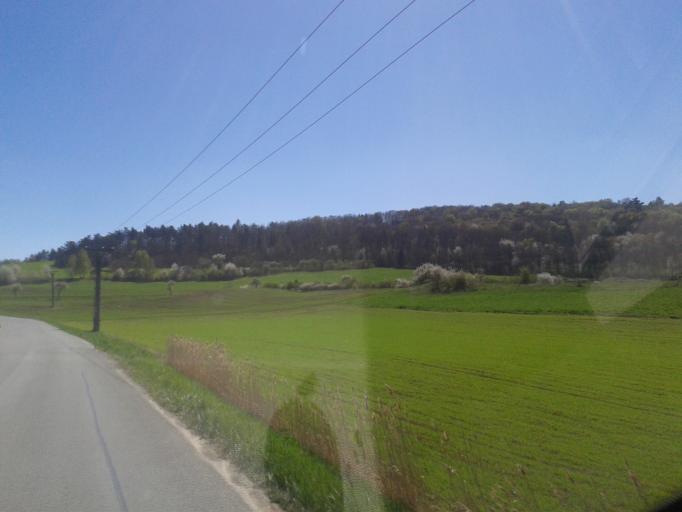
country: CZ
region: Central Bohemia
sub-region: Okres Beroun
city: Beroun
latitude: 49.9216
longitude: 14.0723
